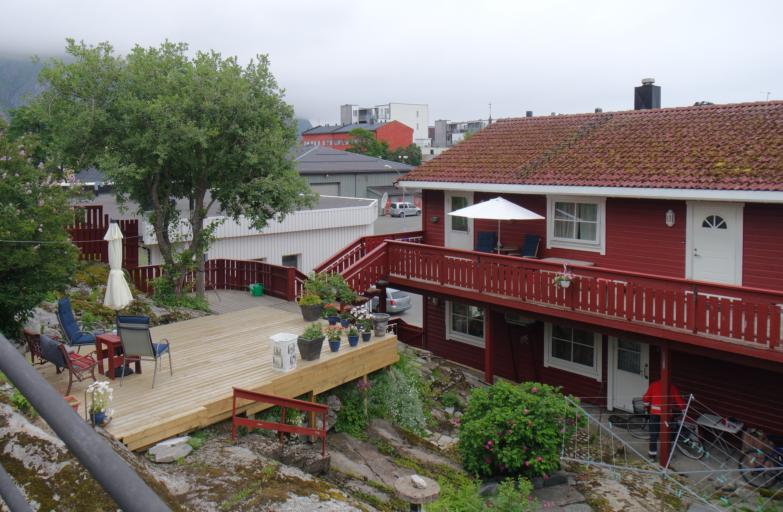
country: NO
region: Nordland
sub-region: Vagan
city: Svolvaer
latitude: 68.2332
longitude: 14.5639
